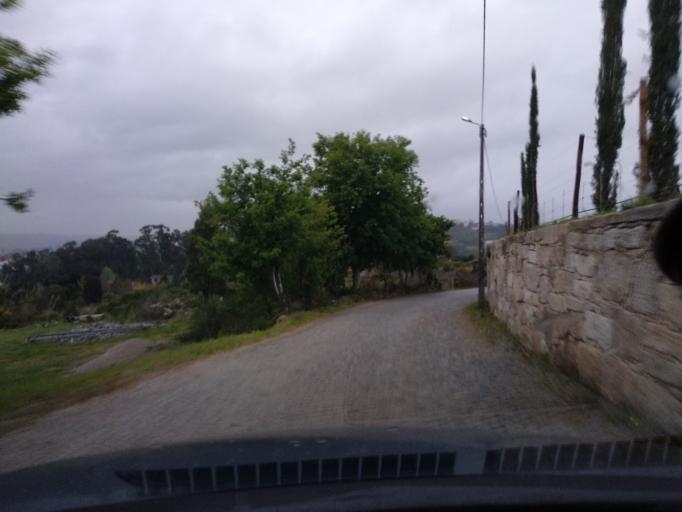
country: PT
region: Porto
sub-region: Penafiel
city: Penafiel
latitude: 41.1856
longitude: -8.2951
